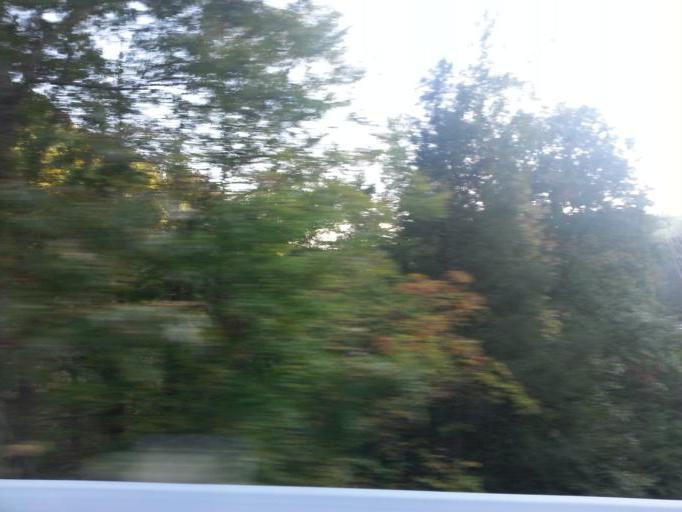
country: US
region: Tennessee
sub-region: Sevier County
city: Pigeon Forge
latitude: 35.6941
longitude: -83.6911
